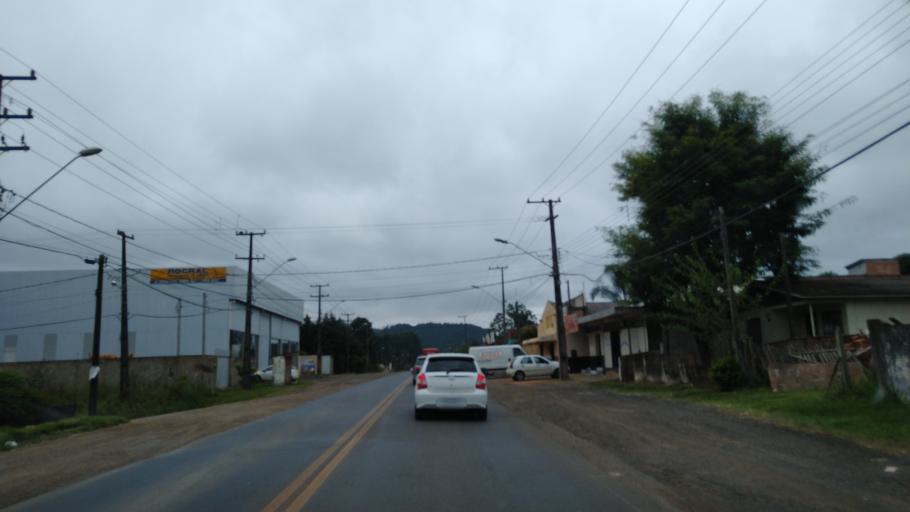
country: BR
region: Parana
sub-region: Uniao Da Vitoria
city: Uniao da Vitoria
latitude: -26.2442
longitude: -51.1224
